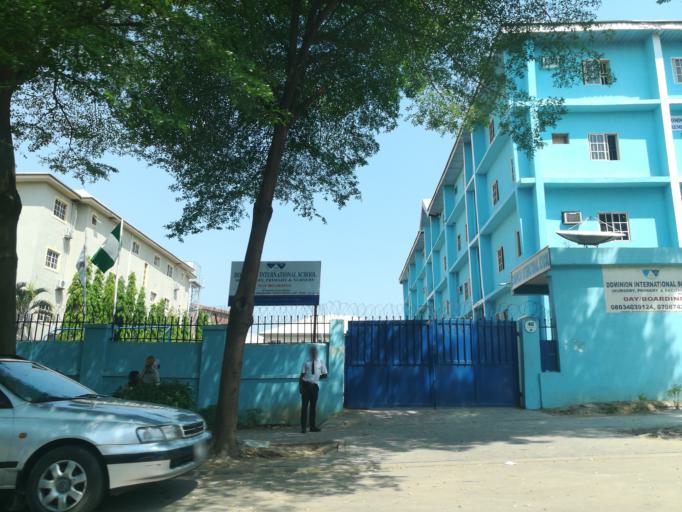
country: NG
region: Abuja Federal Capital Territory
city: Abuja
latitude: 9.0707
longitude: 7.4265
